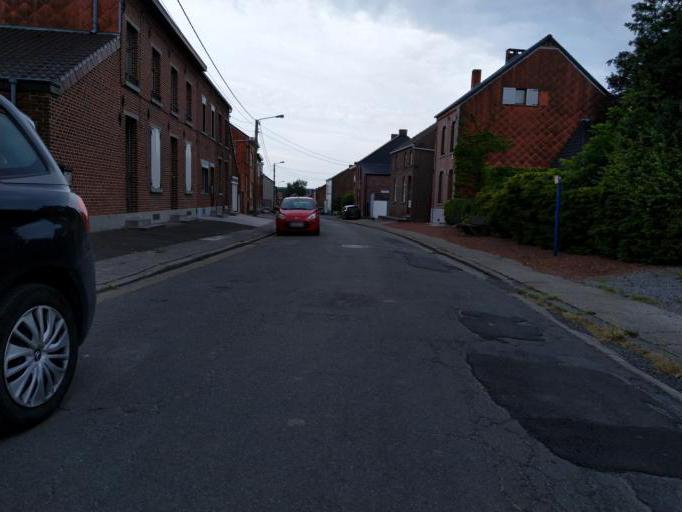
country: BE
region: Wallonia
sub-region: Province du Hainaut
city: Estinnes-au-Val
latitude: 50.4573
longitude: 4.0780
